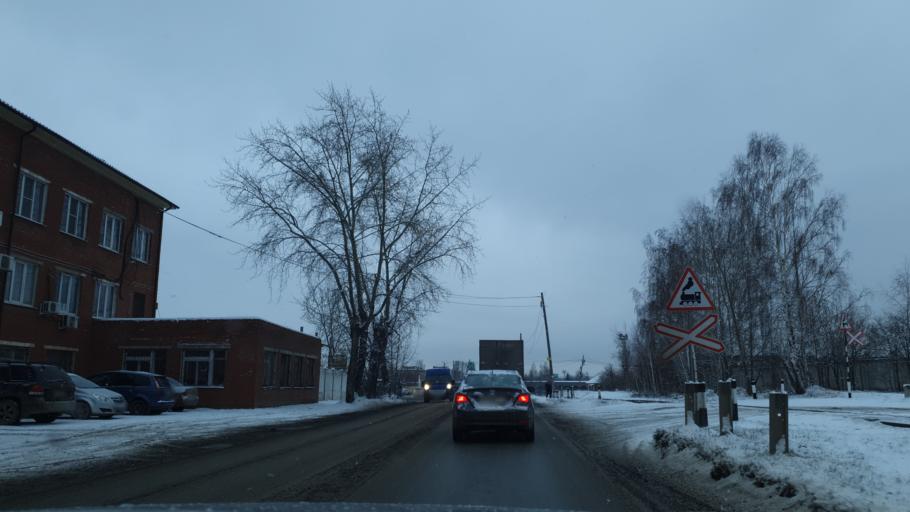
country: RU
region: Sverdlovsk
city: Istok
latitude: 56.7603
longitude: 60.7324
